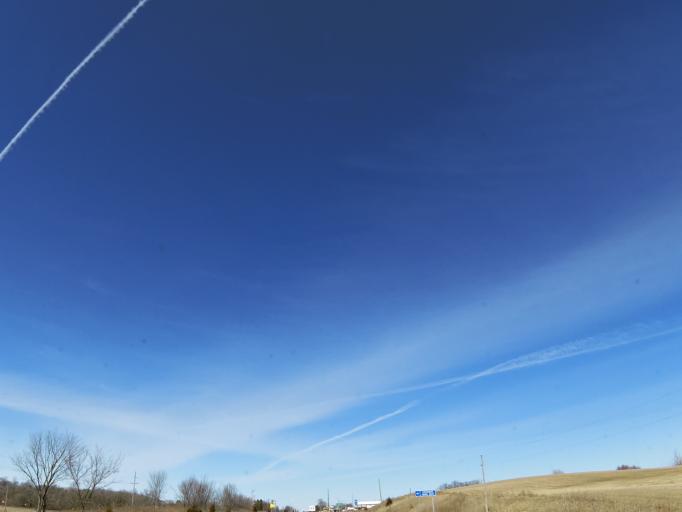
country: US
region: Minnesota
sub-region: Wright County
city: Buffalo
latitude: 45.1340
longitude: -93.8242
